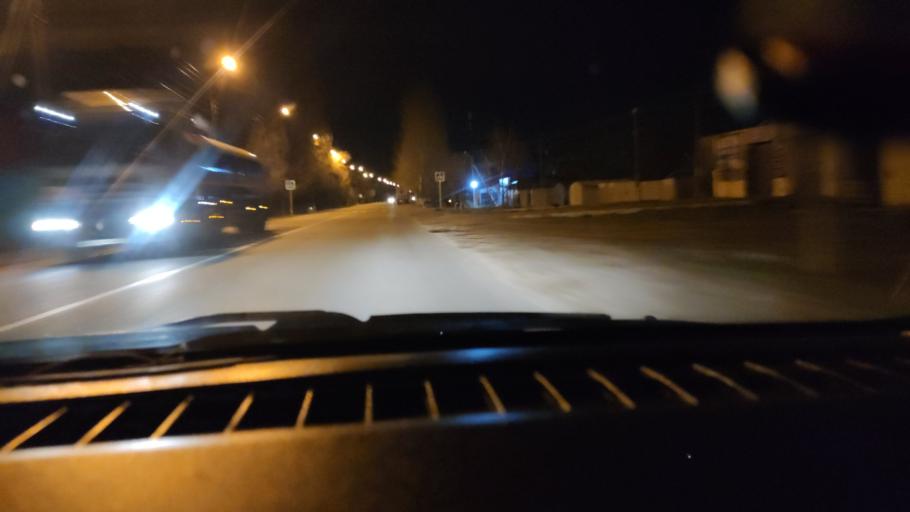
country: RU
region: Saratov
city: Privolzhskiy
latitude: 51.4329
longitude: 46.0570
